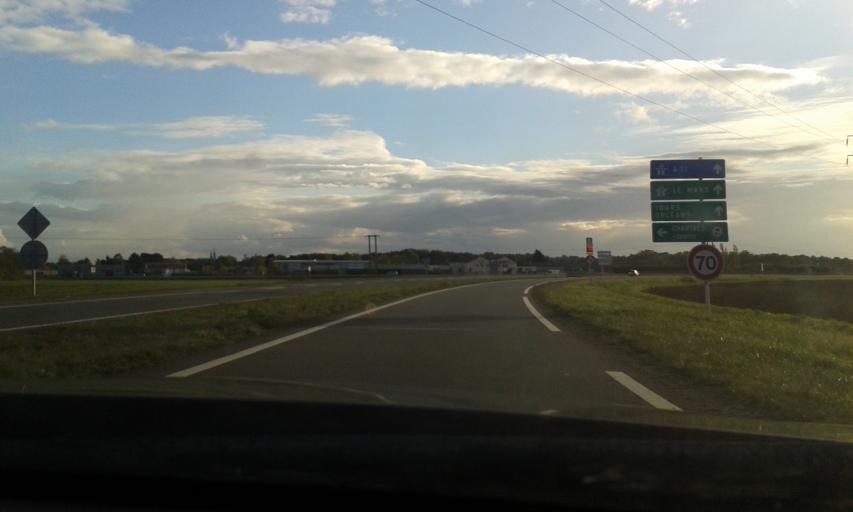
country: FR
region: Centre
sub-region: Departement d'Eure-et-Loir
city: Leves
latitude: 48.4903
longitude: 1.4719
